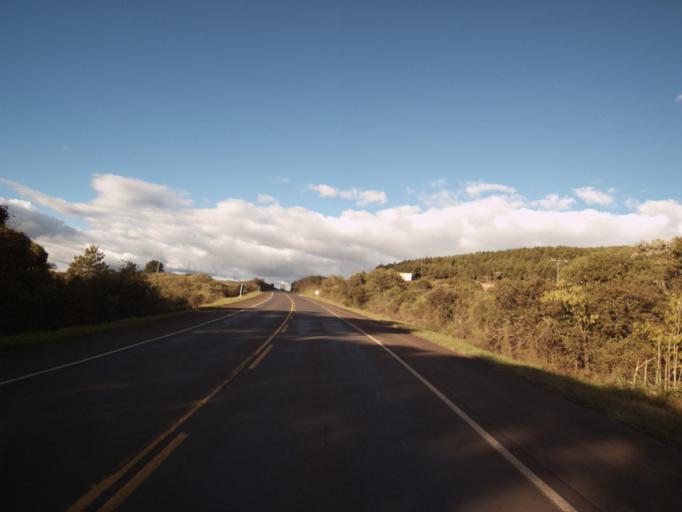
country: BR
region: Santa Catarina
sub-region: Campos Novos
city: Campos Novos
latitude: -27.3595
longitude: -51.3266
